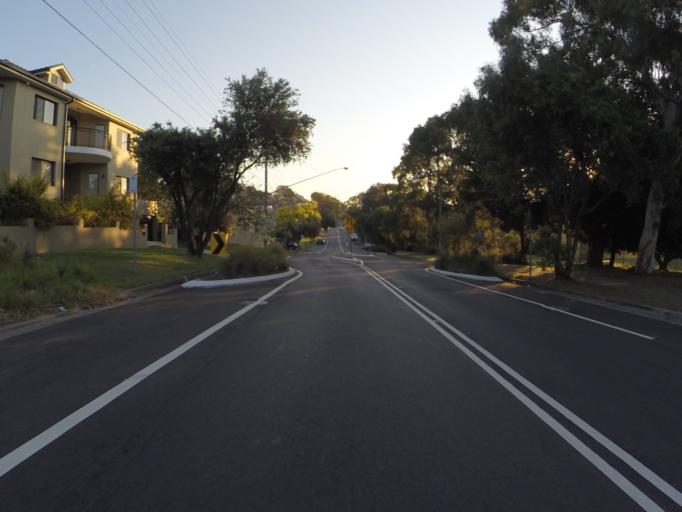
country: AU
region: New South Wales
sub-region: Rockdale
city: Bexley North
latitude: -33.9326
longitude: 151.1242
